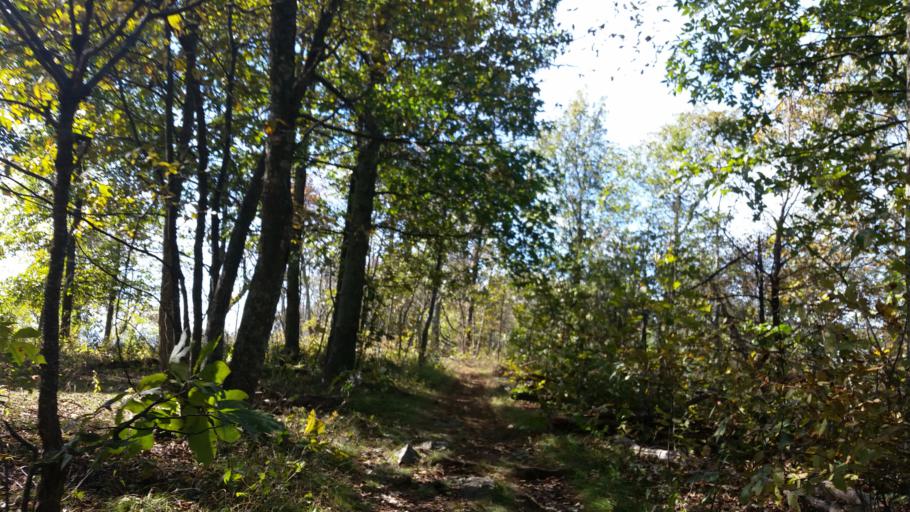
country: US
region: Virginia
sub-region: Shenandoah County
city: Edinburg
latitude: 38.9327
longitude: -78.6725
